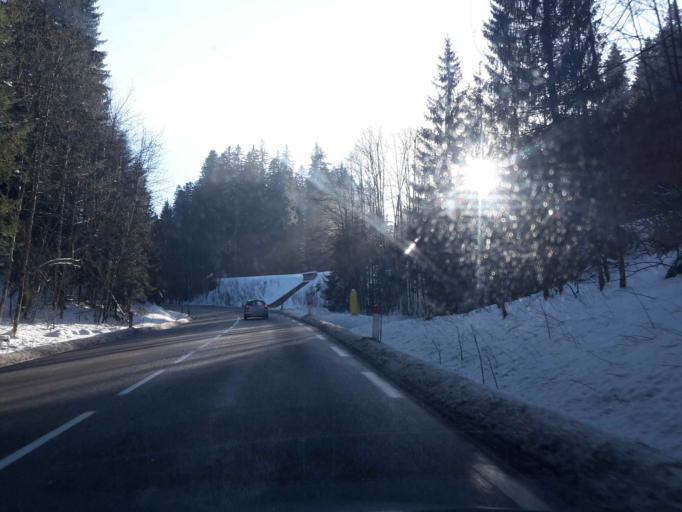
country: FR
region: Franche-Comte
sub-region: Departement du Doubs
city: Les Fourgs
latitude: 46.8115
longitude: 6.3628
